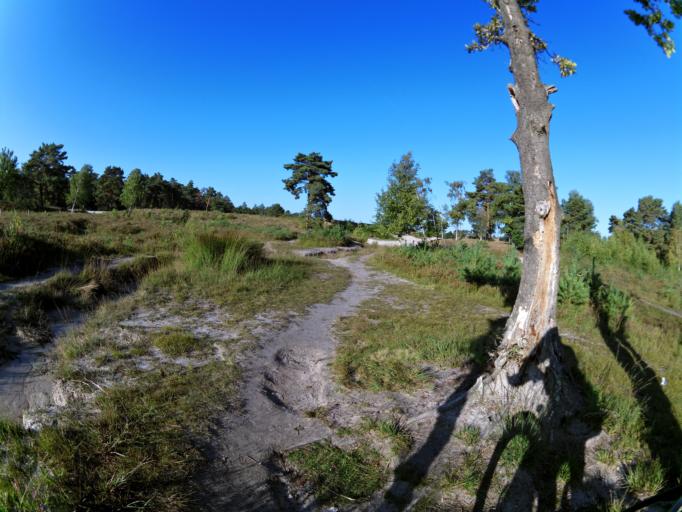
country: NL
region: Limburg
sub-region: Gemeente Brunssum
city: Brunssum
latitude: 50.9289
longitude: 5.9964
